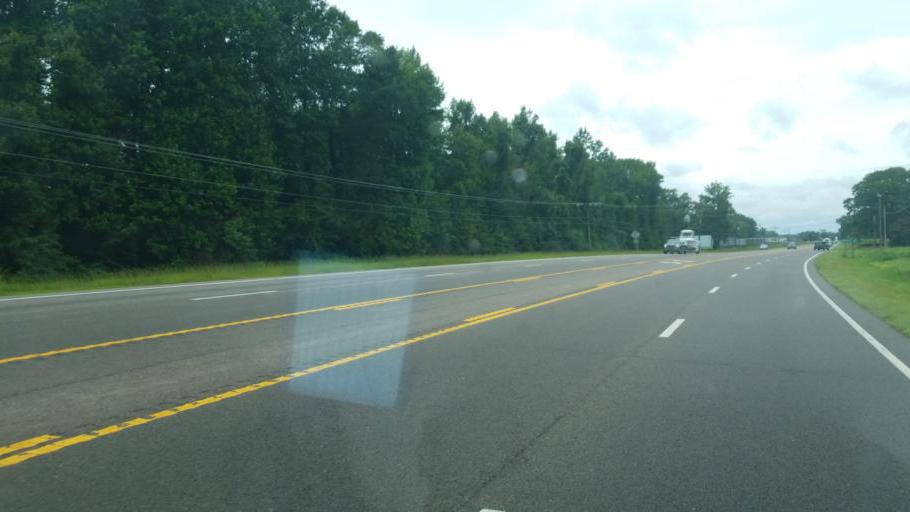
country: US
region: North Carolina
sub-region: Currituck County
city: Currituck
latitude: 36.3194
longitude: -75.9390
